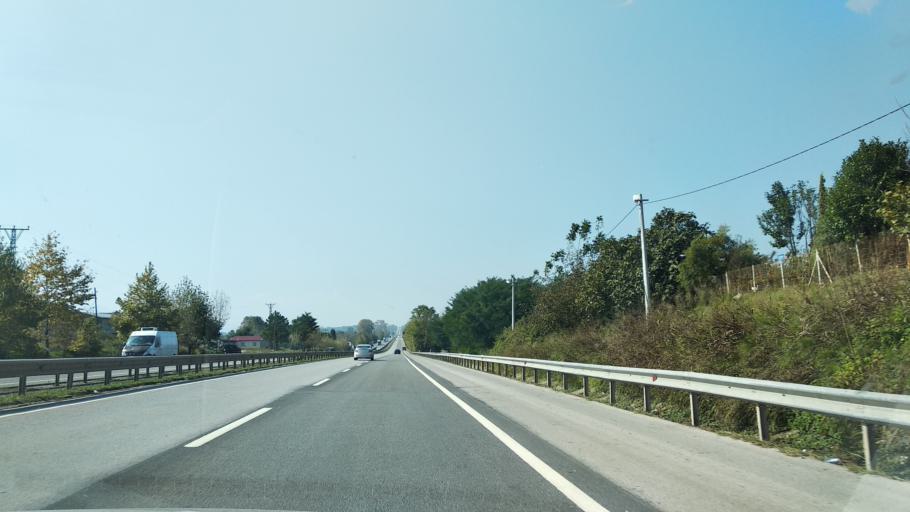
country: TR
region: Sakarya
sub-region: Merkez
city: Sapanca
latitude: 40.7330
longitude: 30.2134
